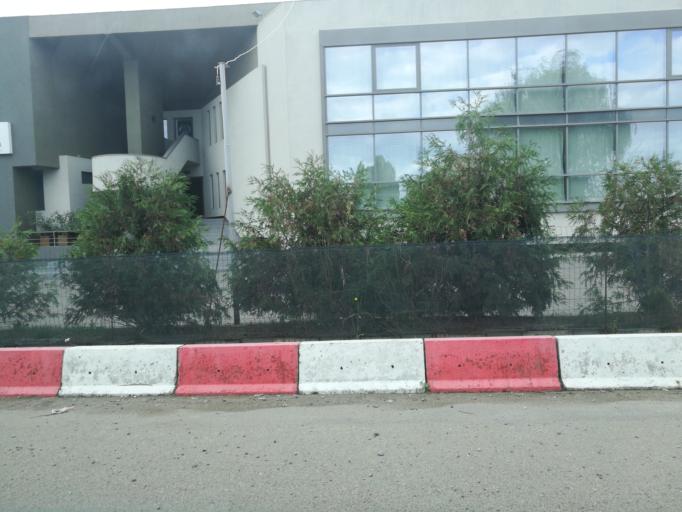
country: RO
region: Mures
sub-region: Comuna Ungheni
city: Ungheni
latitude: 46.4913
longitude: 24.4697
